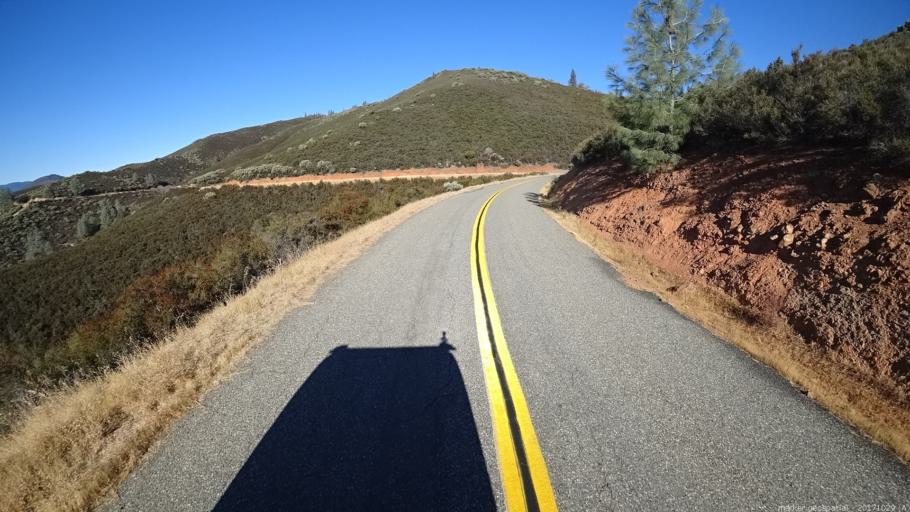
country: US
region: California
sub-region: Trinity County
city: Lewiston
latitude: 40.3648
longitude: -122.8508
